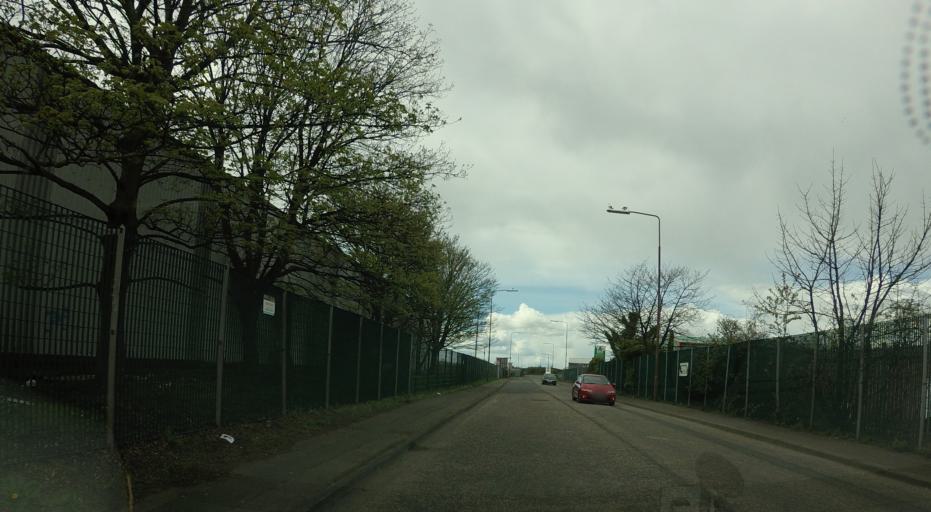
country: GB
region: Scotland
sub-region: Edinburgh
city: Edinburgh
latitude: 55.9824
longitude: -3.2304
